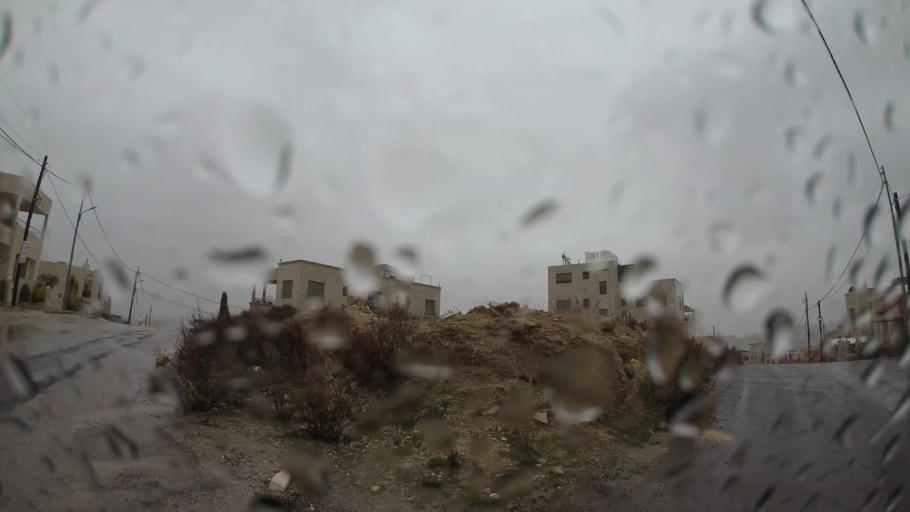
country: JO
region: Amman
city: Al Jubayhah
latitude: 32.0110
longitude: 35.9015
